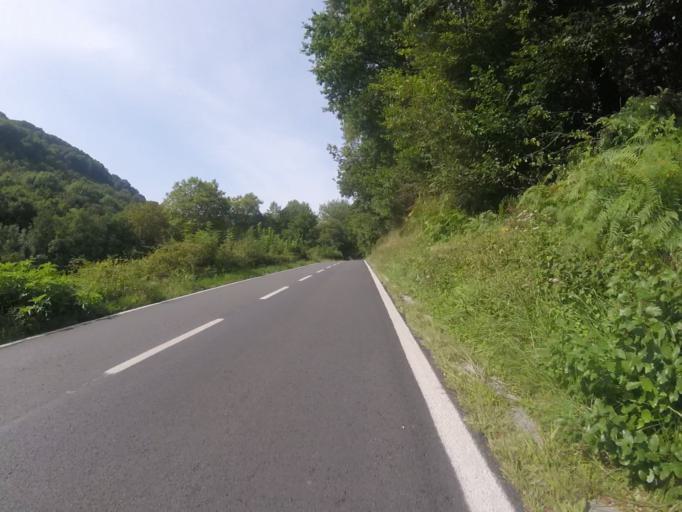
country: ES
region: Navarre
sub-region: Provincia de Navarra
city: Elgorriaga
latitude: 43.1334
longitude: -1.6954
